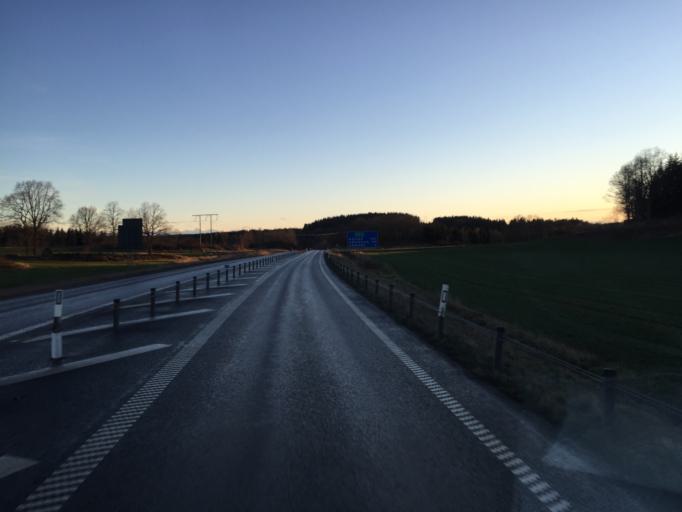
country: SE
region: Kalmar
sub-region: Vasterviks Kommun
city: Gamleby
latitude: 57.9375
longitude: 16.4207
